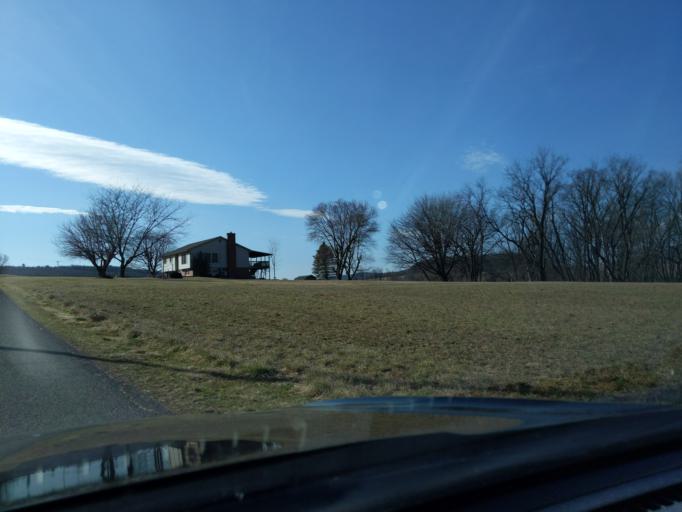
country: US
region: Pennsylvania
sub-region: Blair County
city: Martinsburg
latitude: 40.3935
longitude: -78.2744
